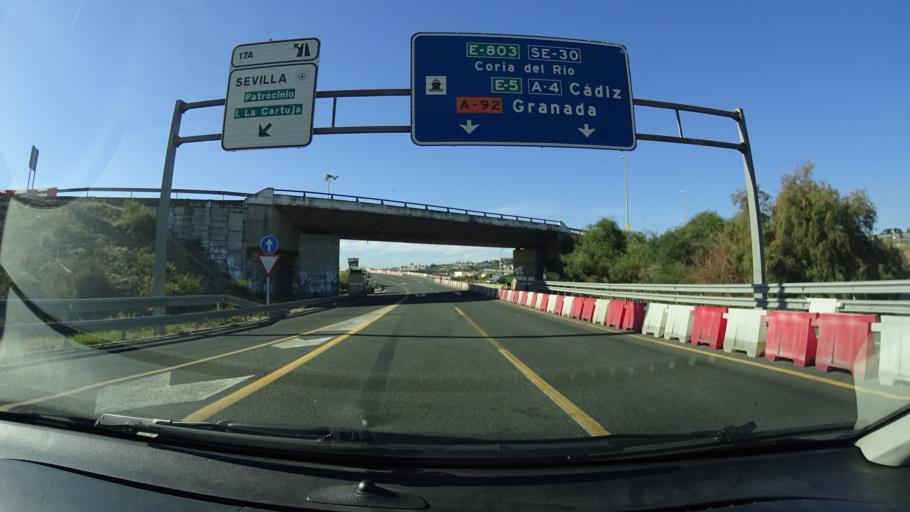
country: ES
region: Andalusia
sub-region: Provincia de Sevilla
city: Camas
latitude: 37.3909
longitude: -6.0267
